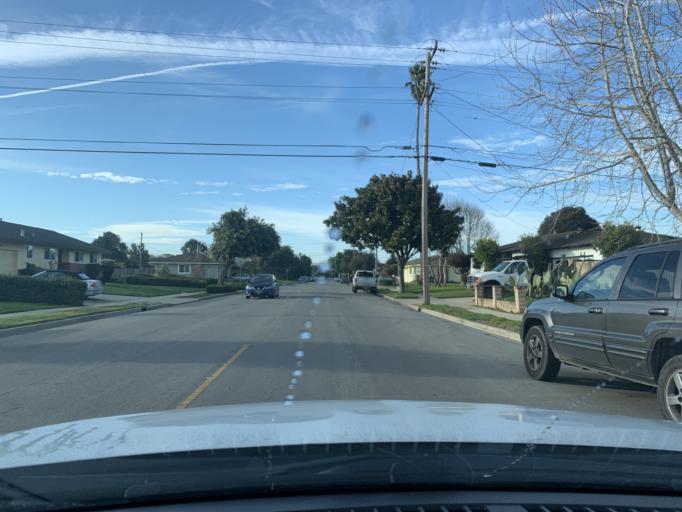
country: US
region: California
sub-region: Monterey County
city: Salinas
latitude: 36.6730
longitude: -121.6761
